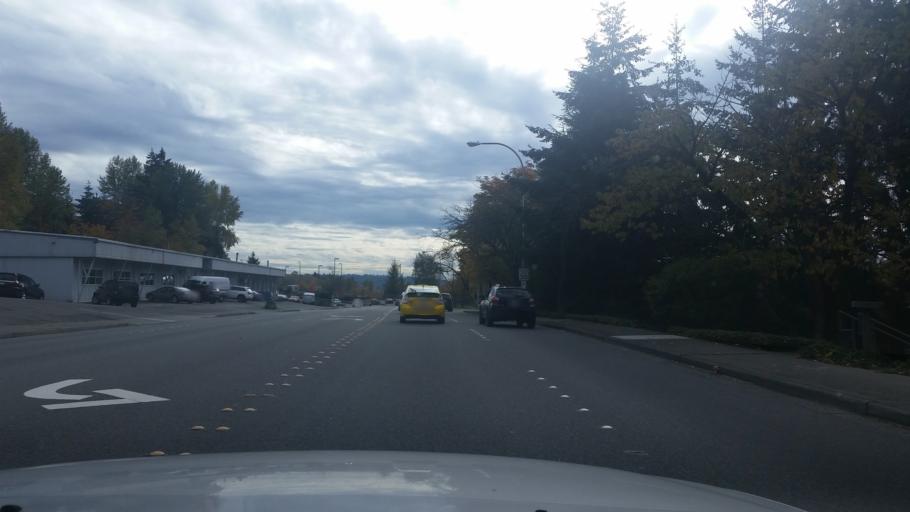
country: US
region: Washington
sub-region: King County
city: Bellevue
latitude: 47.6080
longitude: -122.1855
